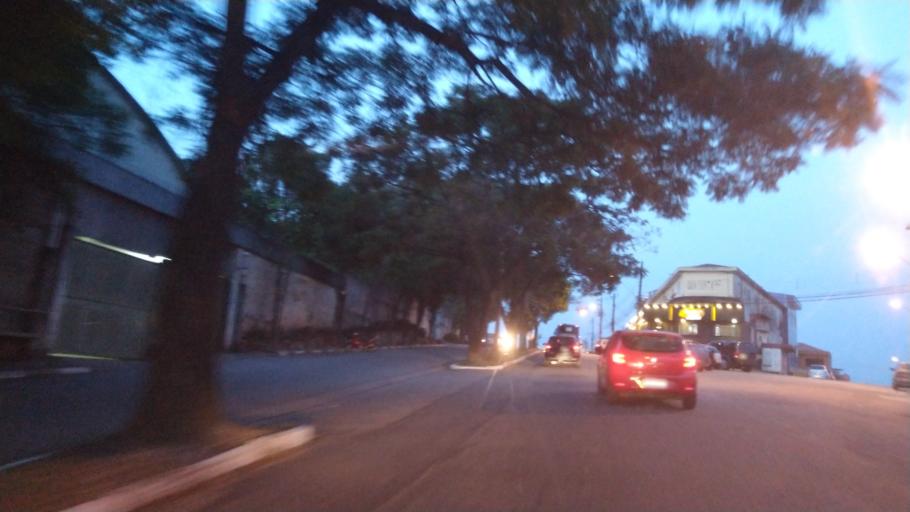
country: BR
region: Sao Paulo
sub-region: Aruja
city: Aruja
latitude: -23.4118
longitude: -46.4037
